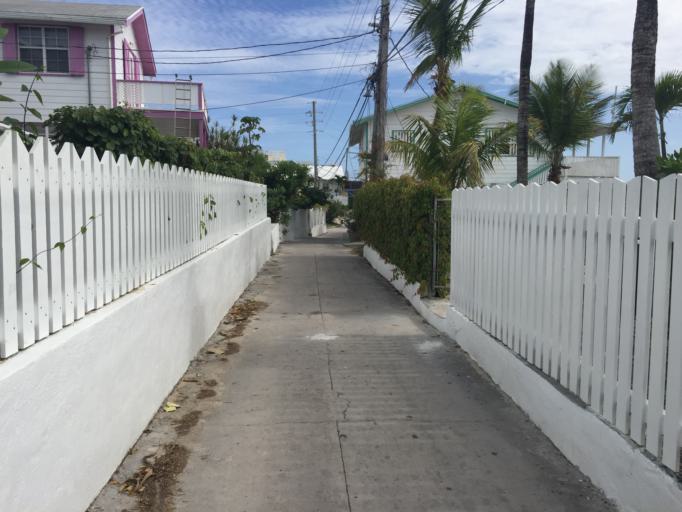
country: BS
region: Central Abaco
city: Marsh Harbour
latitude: 26.5397
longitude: -76.9592
